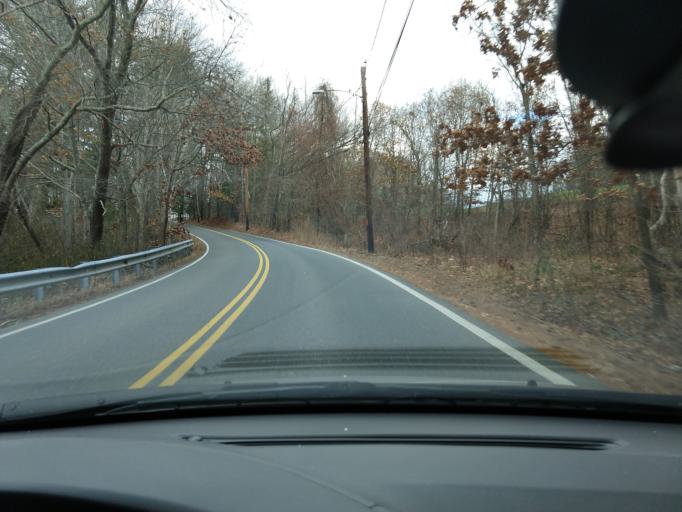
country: US
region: Massachusetts
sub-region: Middlesex County
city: Sudbury
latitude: 42.4101
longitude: -71.3772
